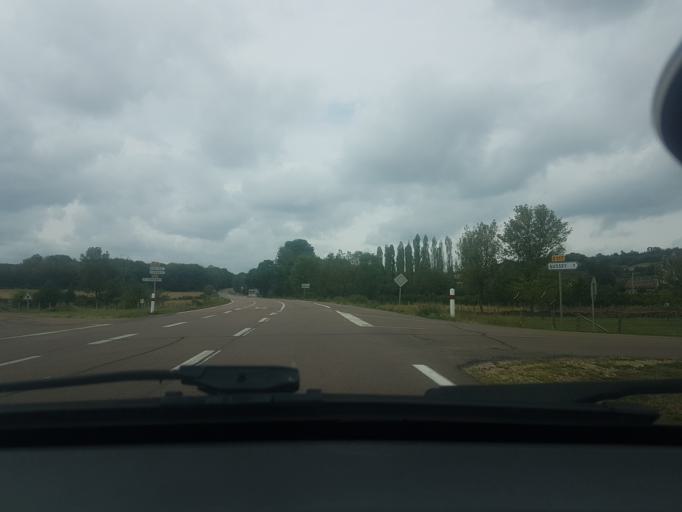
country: FR
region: Bourgogne
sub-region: Departement de la Cote-d'Or
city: Saulieu
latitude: 47.2117
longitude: 4.3572
